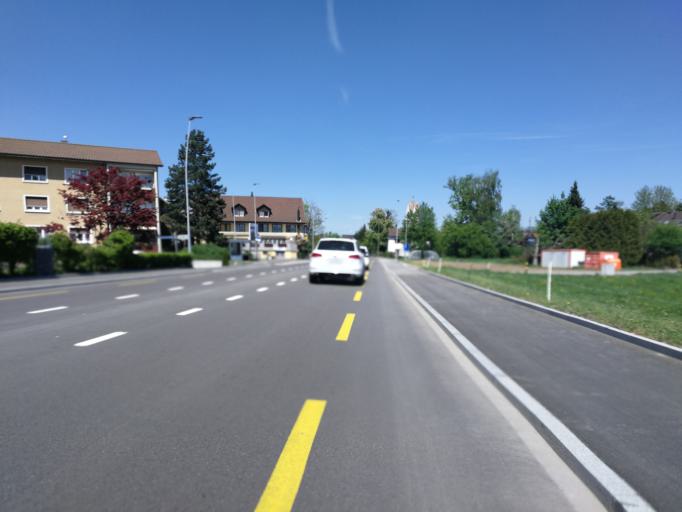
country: CH
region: Zurich
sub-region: Bezirk Uster
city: Monchaltorf
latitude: 47.3077
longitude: 8.7214
